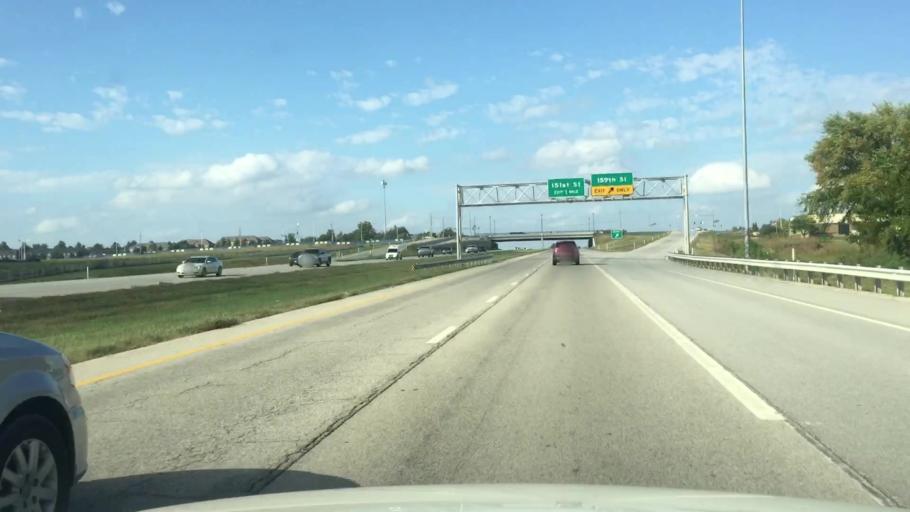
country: US
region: Kansas
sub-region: Johnson County
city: Lenexa
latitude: 38.8355
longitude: -94.6769
